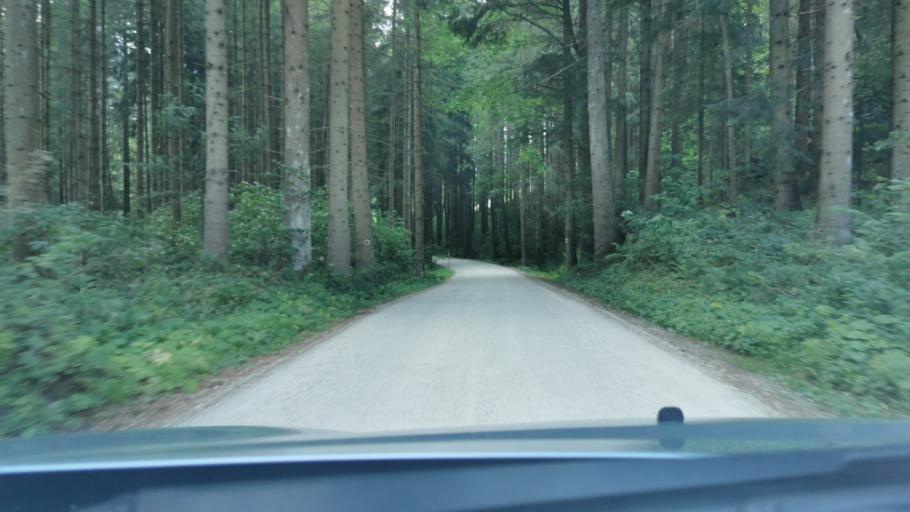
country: AT
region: Styria
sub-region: Politischer Bezirk Weiz
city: Fischbach
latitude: 47.4017
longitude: 15.6453
